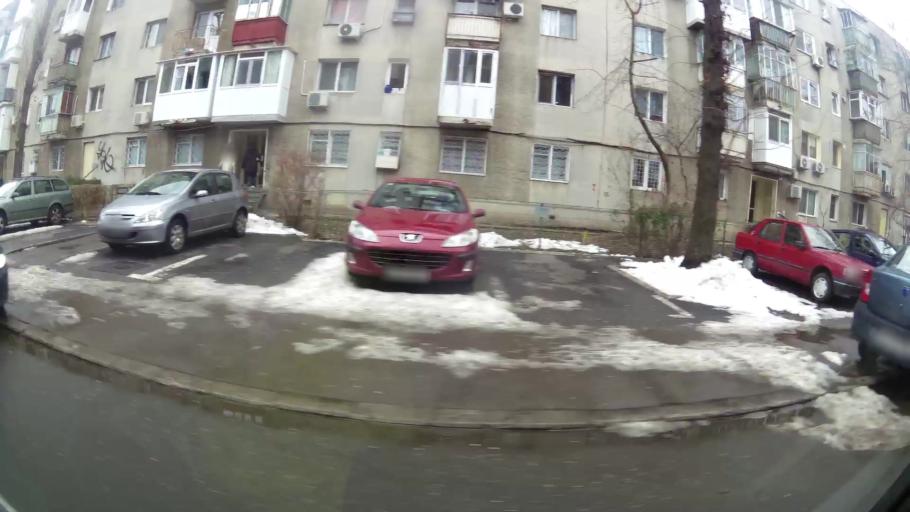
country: RO
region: Ilfov
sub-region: Comuna Popesti-Leordeni
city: Popesti-Leordeni
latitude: 44.4103
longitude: 26.1440
